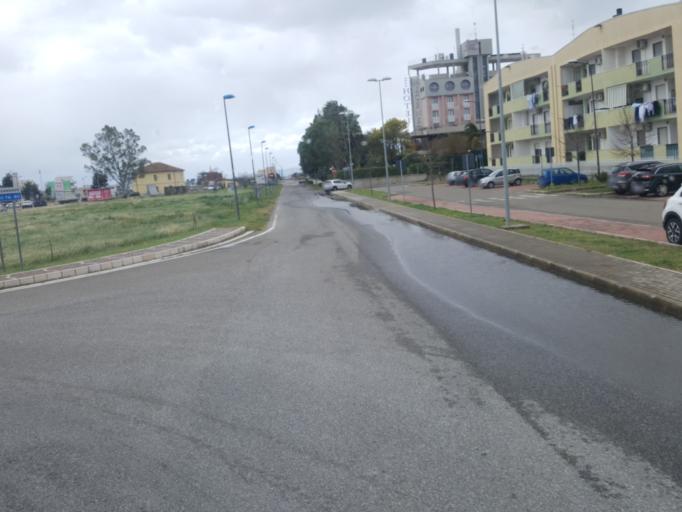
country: IT
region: Basilicate
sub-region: Provincia di Matera
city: Scanzano Jonico
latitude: 40.2506
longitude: 16.6982
